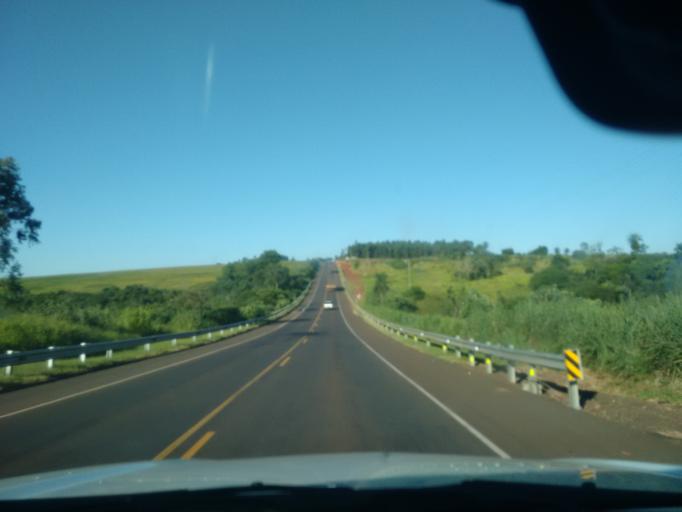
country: PY
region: Canindeyu
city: Salto del Guaira
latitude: -23.9664
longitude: -54.3261
